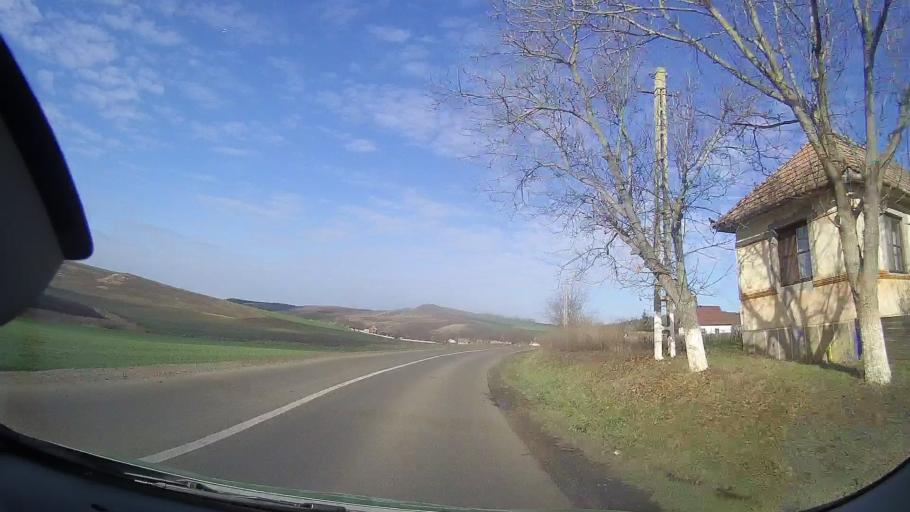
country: RO
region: Mures
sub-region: Comuna Grebenisu de Campie
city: Grebenisu de Campie
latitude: 46.6099
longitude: 24.2587
